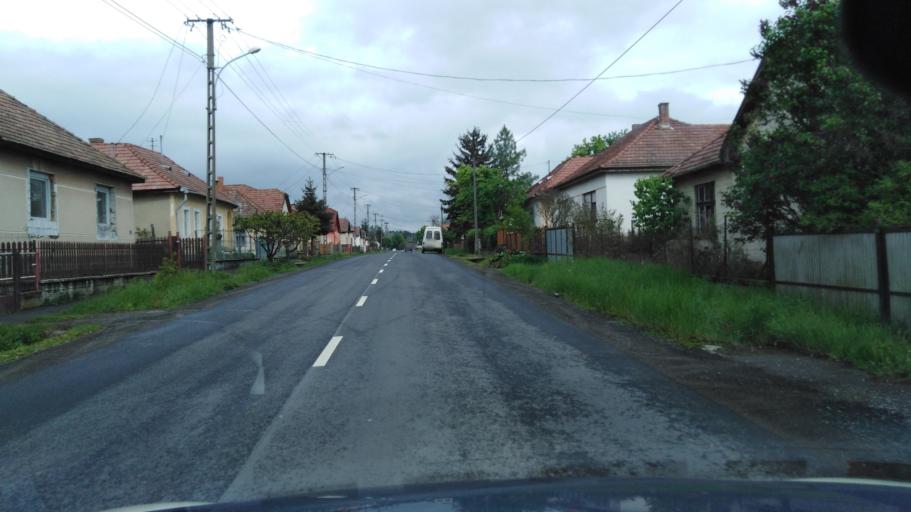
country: HU
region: Nograd
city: Szecseny
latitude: 48.1266
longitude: 19.5690
